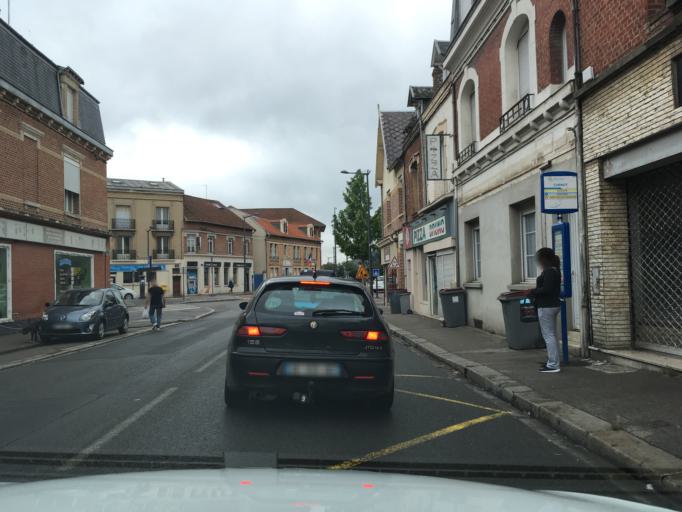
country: FR
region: Picardie
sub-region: Departement de l'Aisne
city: Harly
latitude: 49.8395
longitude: 3.3012
